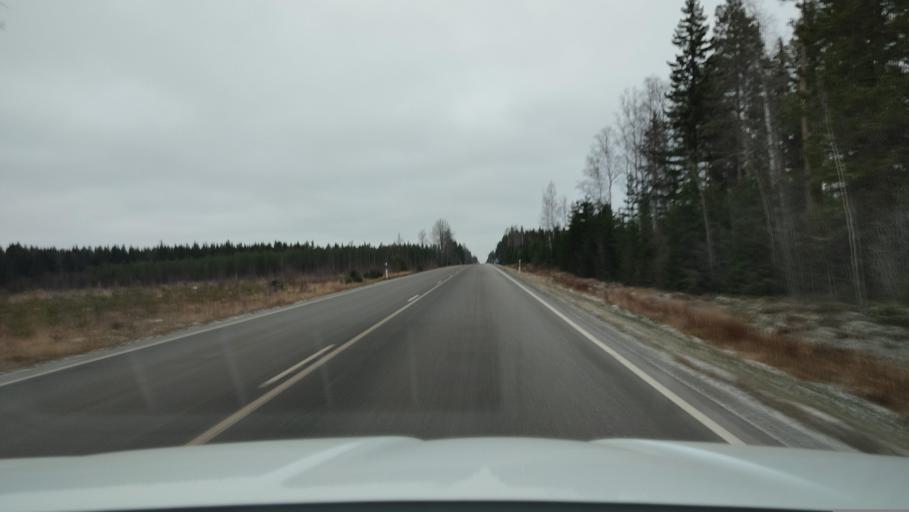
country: FI
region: Ostrobothnia
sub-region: Sydosterbotten
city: Naerpes
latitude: 62.4968
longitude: 21.4469
